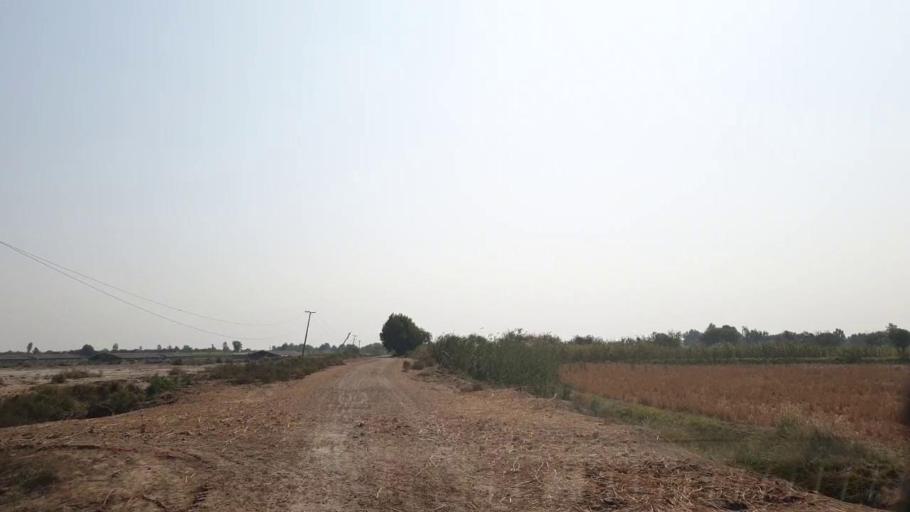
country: PK
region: Sindh
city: Tando Muhammad Khan
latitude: 25.0439
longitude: 68.4529
